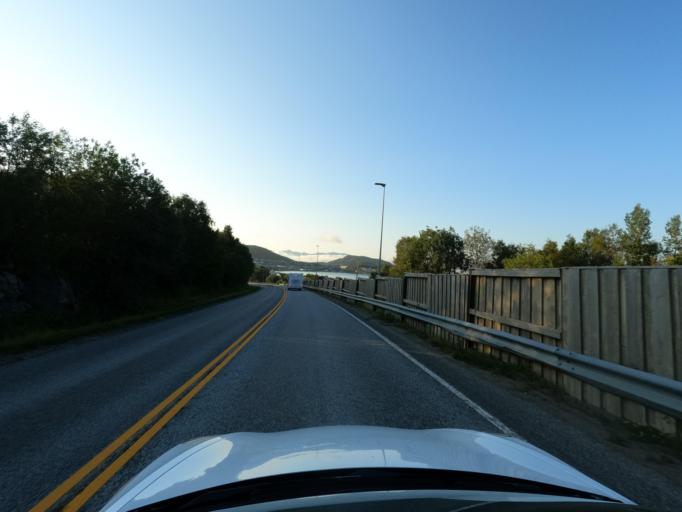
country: NO
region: Troms
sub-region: Harstad
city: Harstad
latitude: 68.7583
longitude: 16.5681
